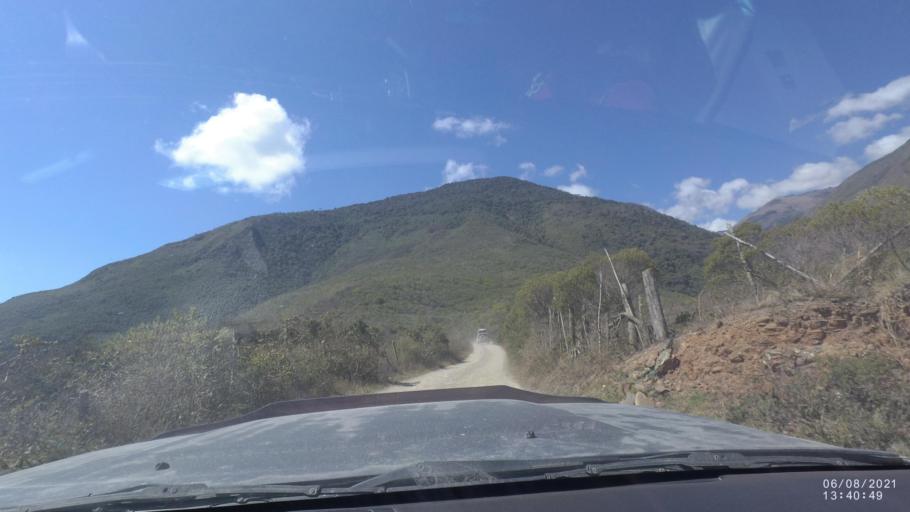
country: BO
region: La Paz
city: Quime
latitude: -16.6848
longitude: -66.7329
